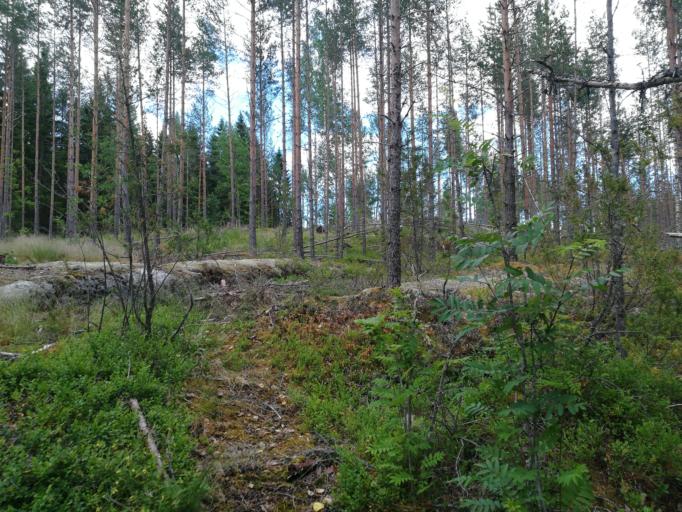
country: FI
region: Southern Savonia
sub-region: Mikkeli
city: Hirvensalmi
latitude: 61.7067
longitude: 26.9715
